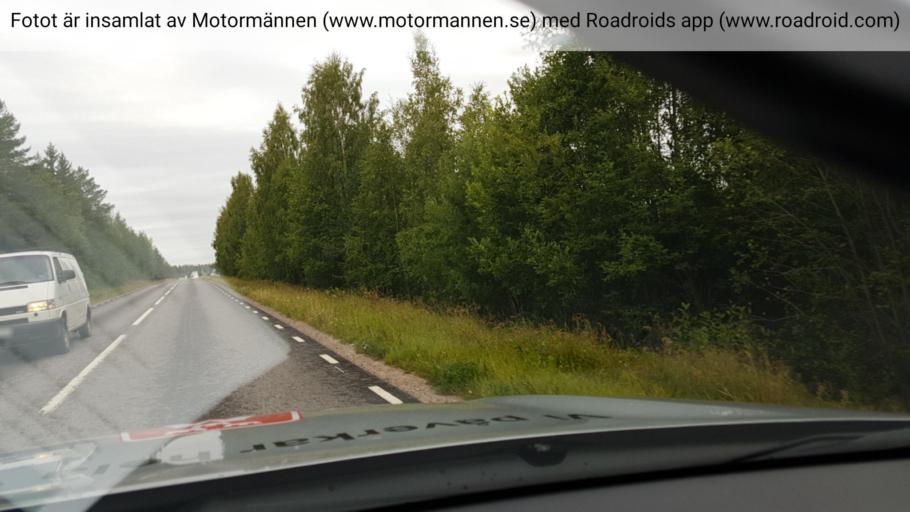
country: SE
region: Norrbotten
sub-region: Lulea Kommun
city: Sodra Sunderbyn
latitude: 65.6594
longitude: 21.8363
